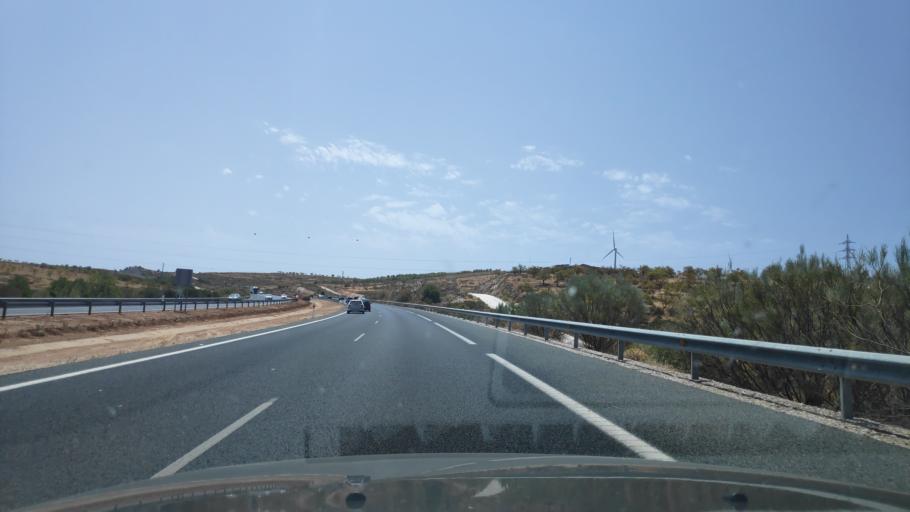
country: ES
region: Andalusia
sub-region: Provincia de Granada
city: Padul
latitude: 37.0099
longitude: -3.6403
